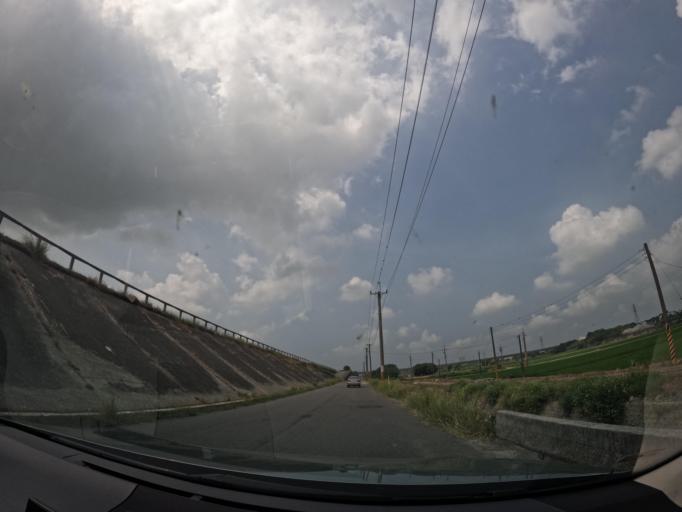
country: TW
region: Taiwan
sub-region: Chiayi
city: Taibao
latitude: 23.5956
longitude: 120.3397
